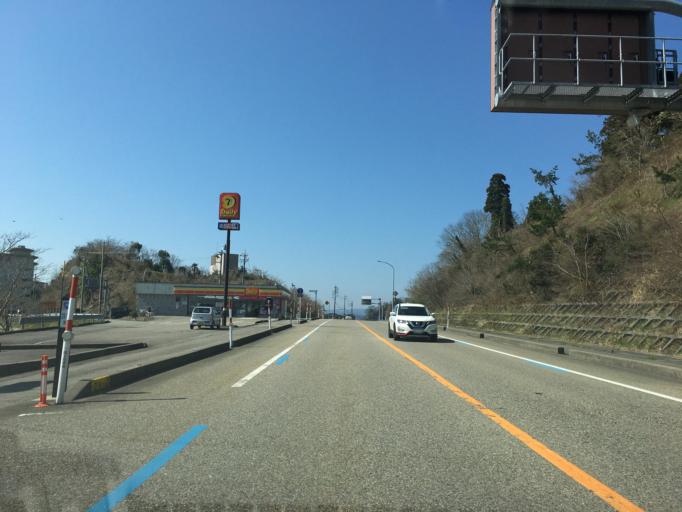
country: JP
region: Toyama
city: Himi
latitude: 36.8876
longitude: 136.9977
